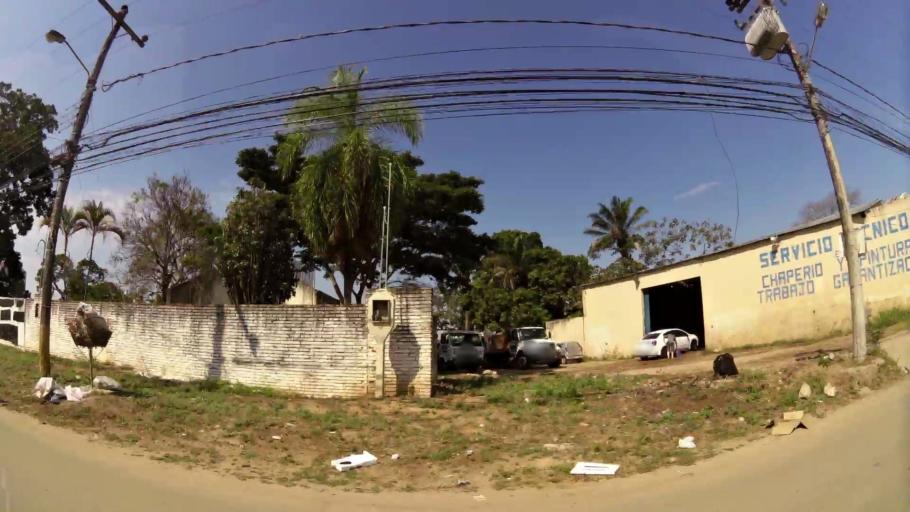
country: BO
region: Santa Cruz
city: Santa Cruz de la Sierra
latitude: -17.7446
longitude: -63.1712
